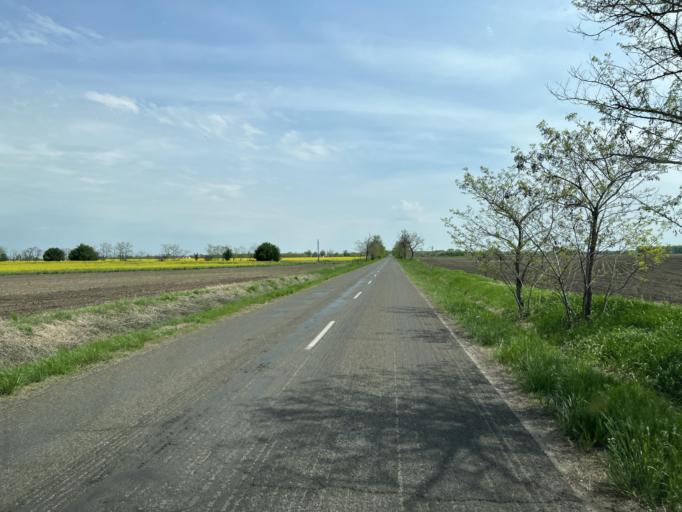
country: HU
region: Pest
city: Tapiogyorgye
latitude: 47.3355
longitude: 19.9168
